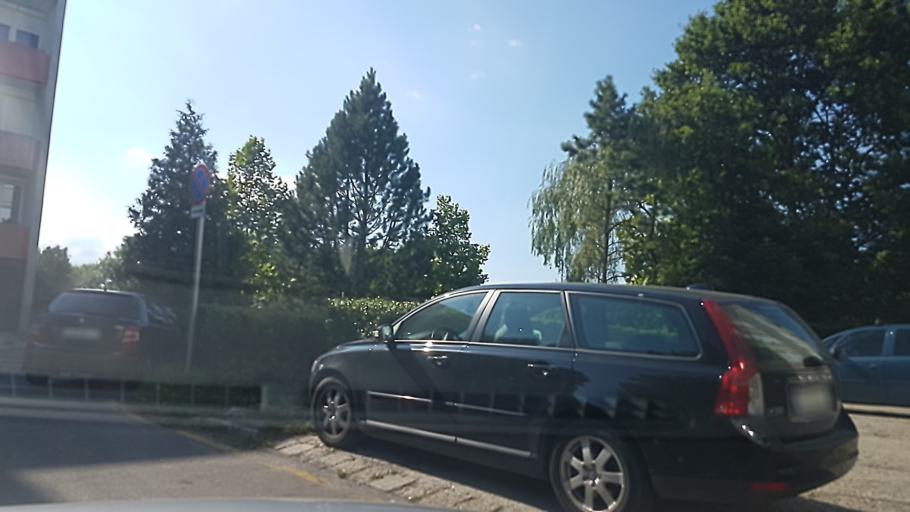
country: HU
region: Gyor-Moson-Sopron
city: Sopron
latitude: 47.6964
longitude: 16.5731
